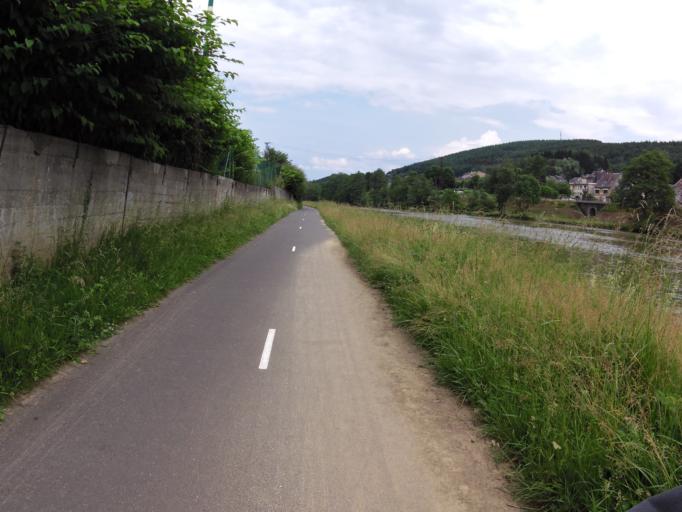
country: FR
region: Champagne-Ardenne
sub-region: Departement des Ardennes
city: Nouzonville
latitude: 49.8186
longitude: 4.7420
